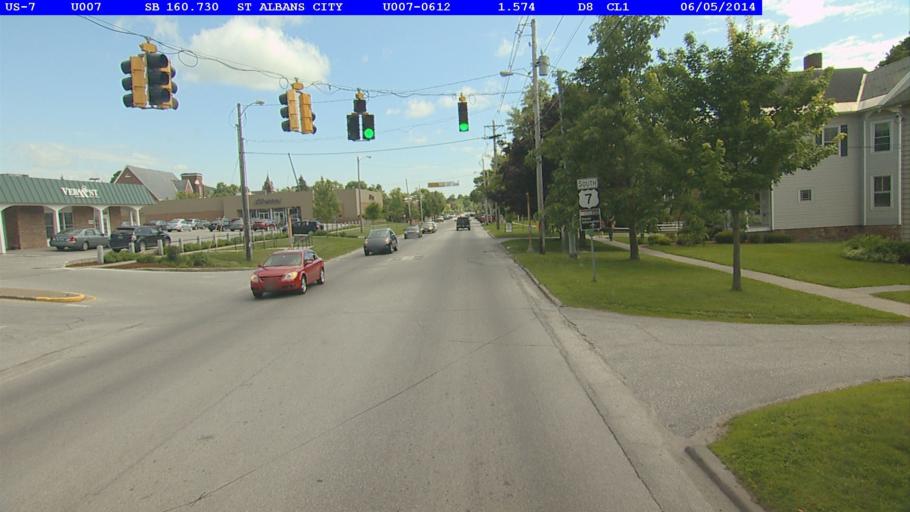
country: US
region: Vermont
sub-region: Franklin County
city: Saint Albans
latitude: 44.8154
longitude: -73.0826
